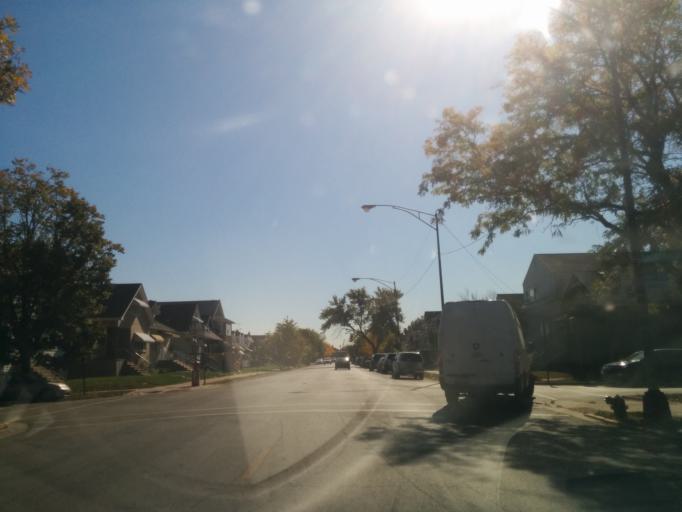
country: US
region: Illinois
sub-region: Cook County
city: Elmwood Park
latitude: 41.9203
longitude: -87.7853
